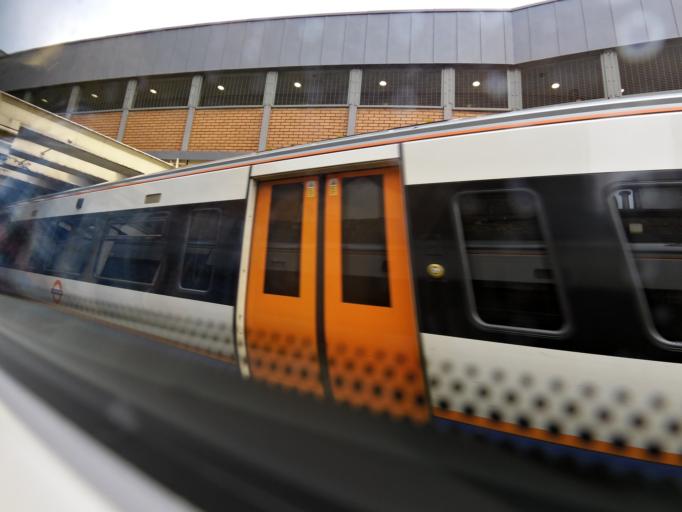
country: GB
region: England
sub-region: Greater London
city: Poplar
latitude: 51.4935
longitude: -0.0473
